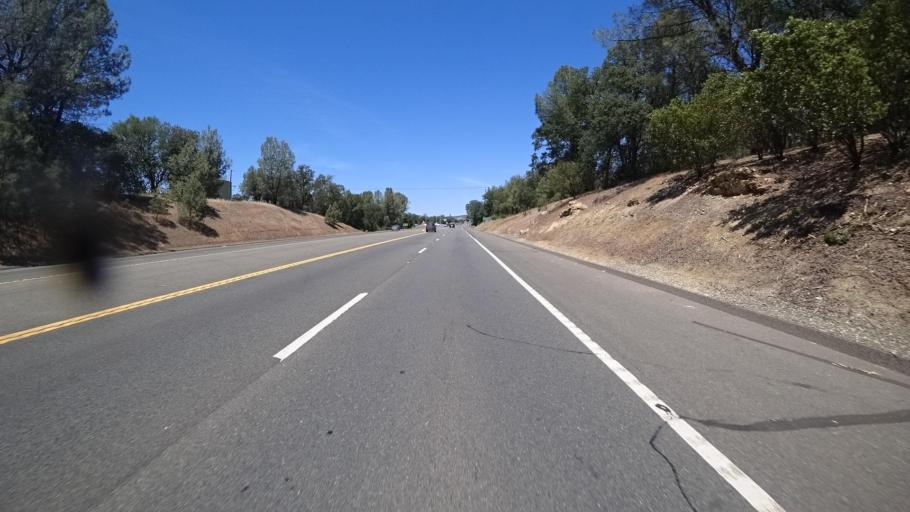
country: US
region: California
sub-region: Lake County
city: Clearlake
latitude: 38.9473
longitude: -122.6232
